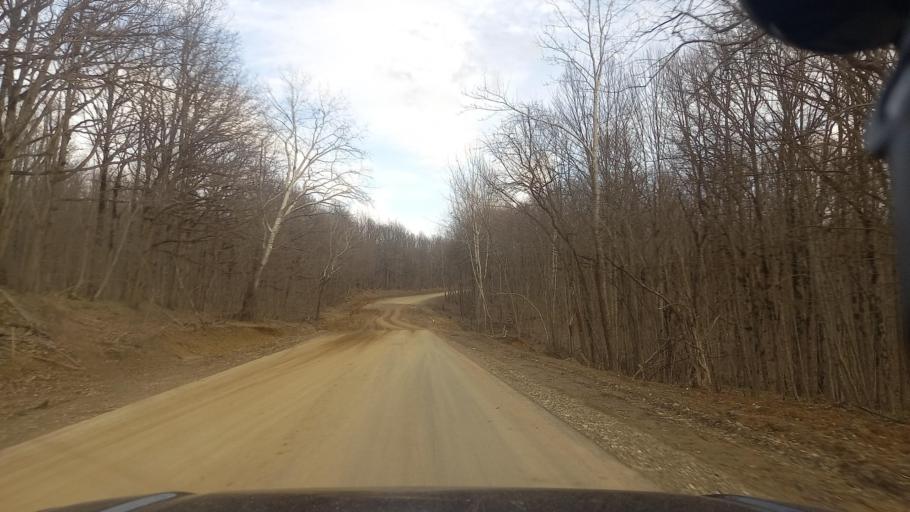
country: RU
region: Krasnodarskiy
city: Goryachiy Klyuch
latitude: 44.7005
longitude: 39.0181
